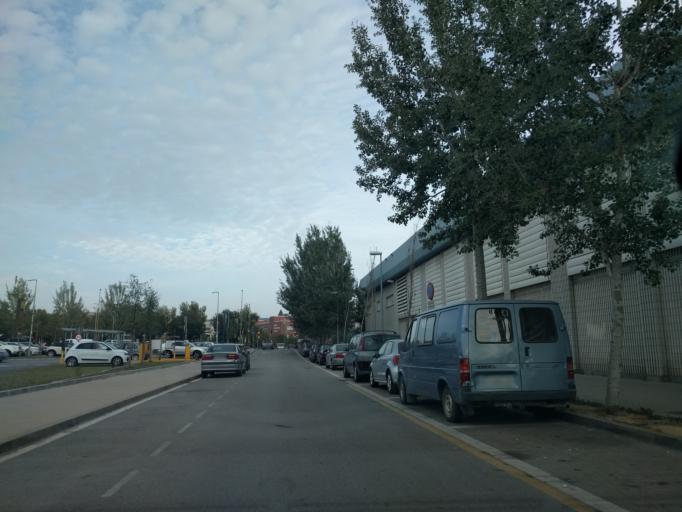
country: ES
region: Catalonia
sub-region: Provincia de Girona
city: Girona
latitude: 41.9812
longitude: 2.8095
